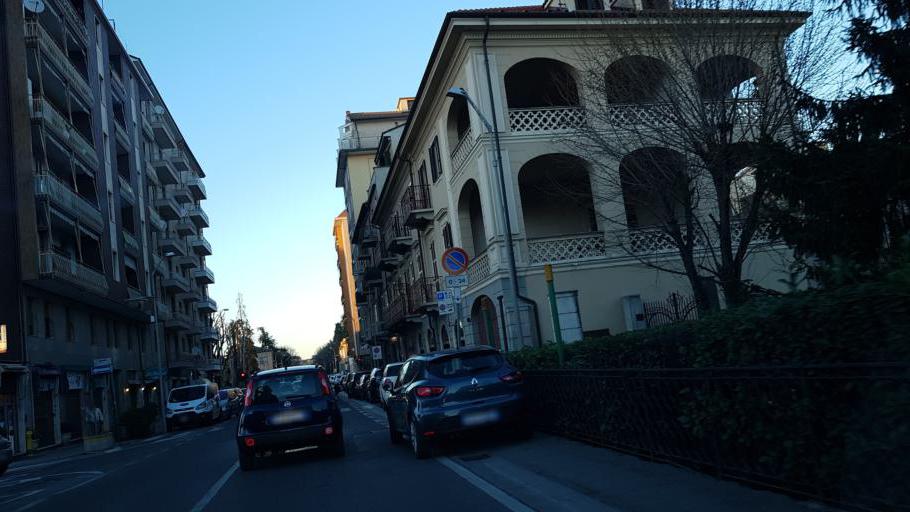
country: IT
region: Piedmont
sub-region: Provincia di Alessandria
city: Tortona
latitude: 44.8901
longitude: 8.8601
